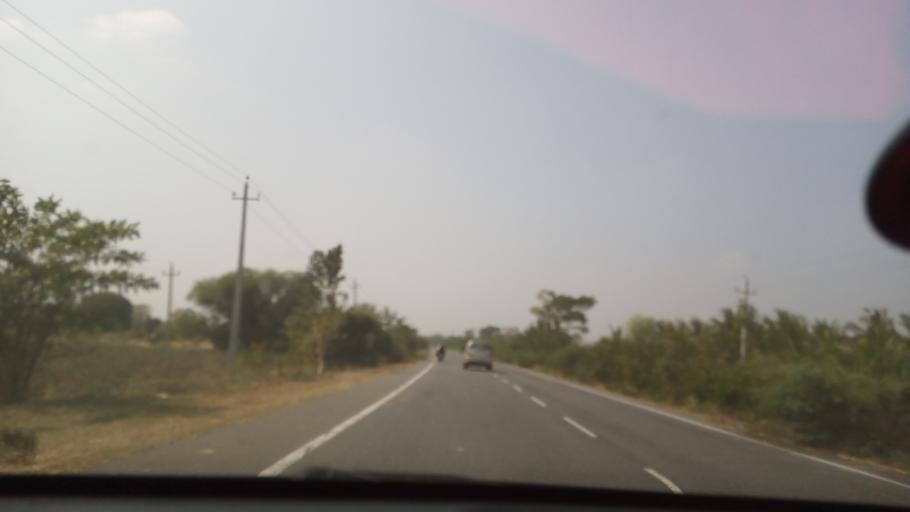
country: IN
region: Karnataka
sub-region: Mysore
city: Nanjangud
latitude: 12.0595
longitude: 76.7639
